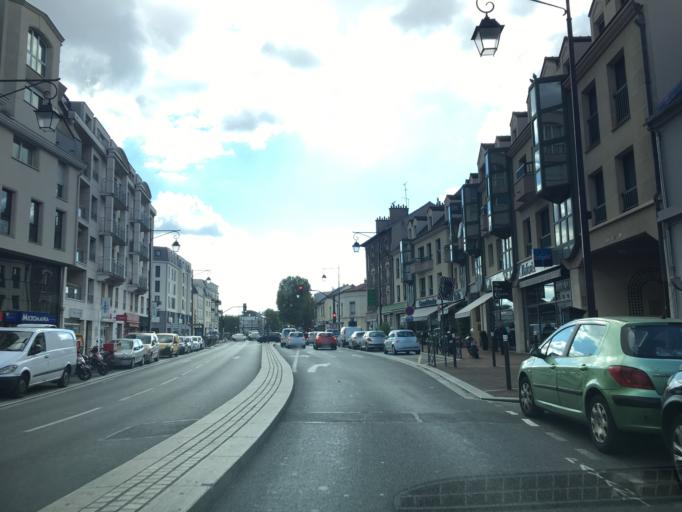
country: FR
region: Ile-de-France
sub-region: Departement des Hauts-de-Seine
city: Antony
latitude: 48.7521
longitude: 2.3046
